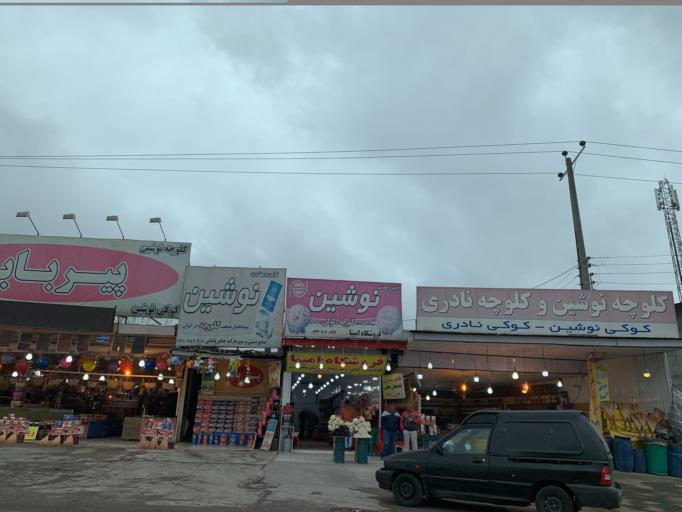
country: IR
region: Mazandaran
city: Amol
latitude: 36.4645
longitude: 52.3945
